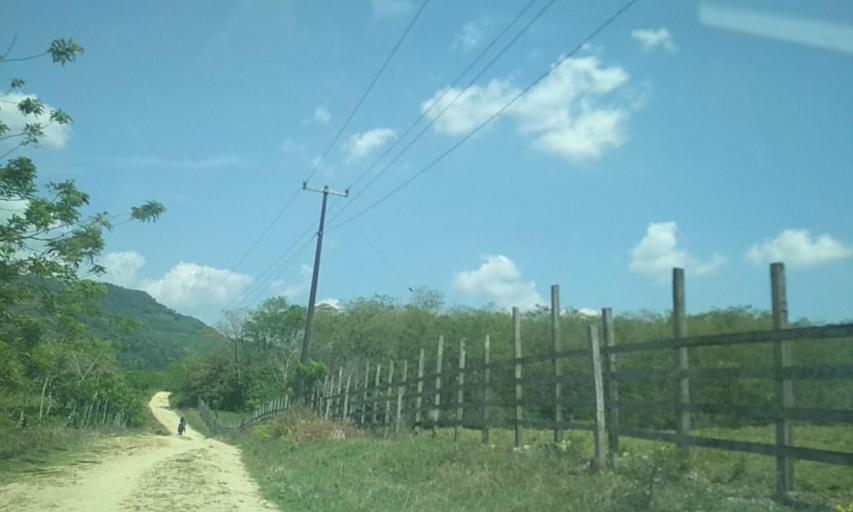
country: MX
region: Chiapas
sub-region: Tecpatan
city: Raudales Malpaso
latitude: 17.2993
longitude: -93.8135
